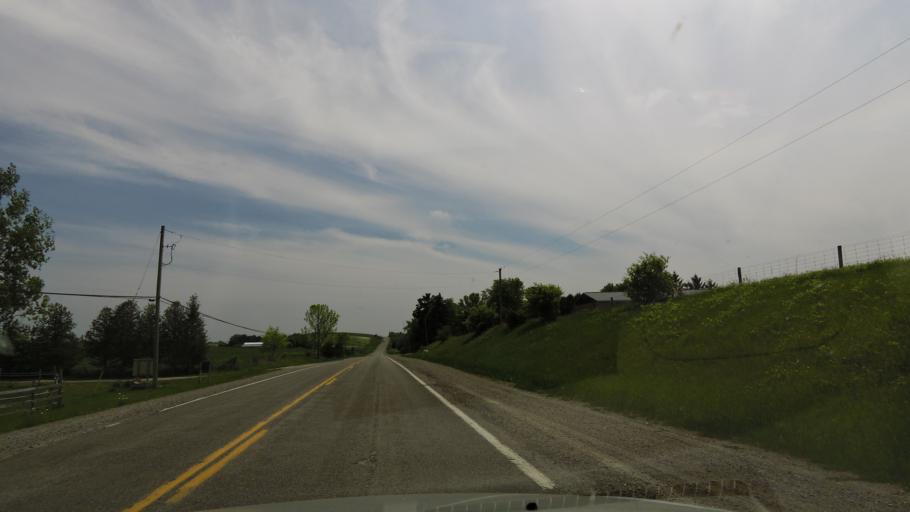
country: CA
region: Ontario
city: Omemee
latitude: 43.9694
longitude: -78.5062
